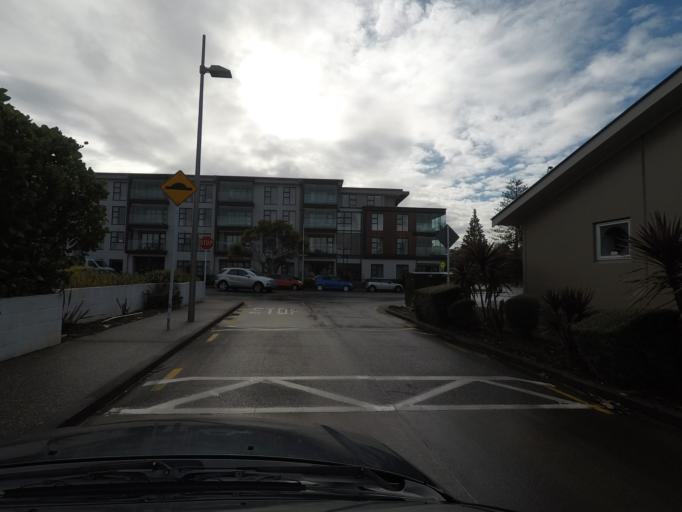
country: NZ
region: Auckland
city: Murrays Bay
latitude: -36.7133
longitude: 174.7491
